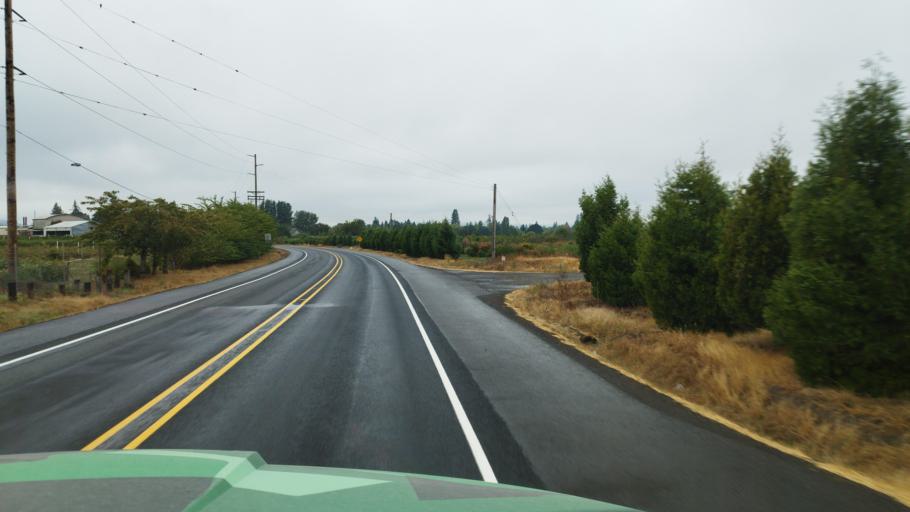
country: US
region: Oregon
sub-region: Washington County
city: Cornelius
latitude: 45.5370
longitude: -123.0773
